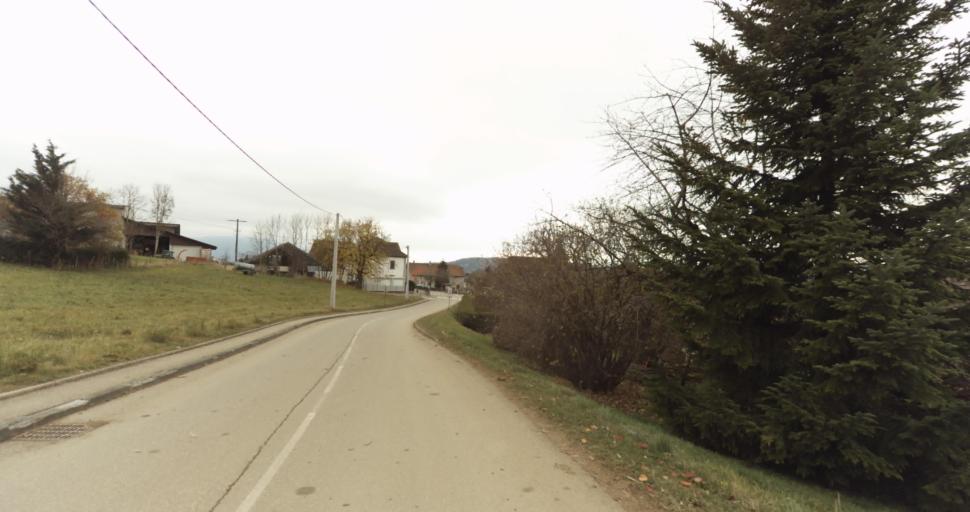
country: FR
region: Rhone-Alpes
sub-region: Departement de la Haute-Savoie
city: Villaz
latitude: 45.9795
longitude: 6.1830
